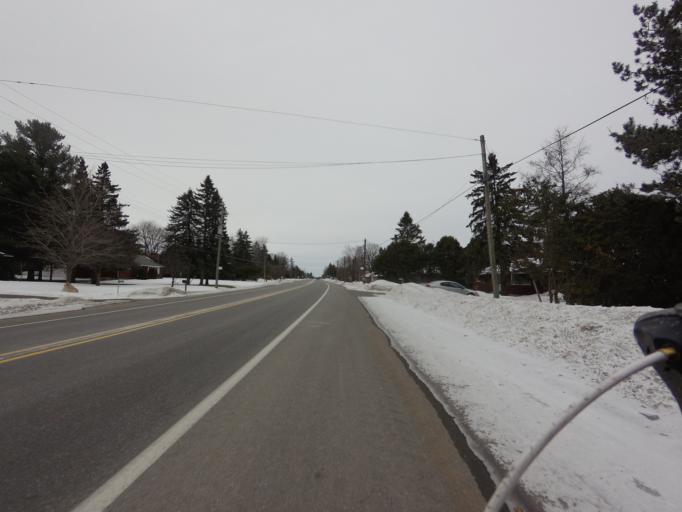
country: CA
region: Ontario
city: Bells Corners
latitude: 45.2546
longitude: -75.6985
